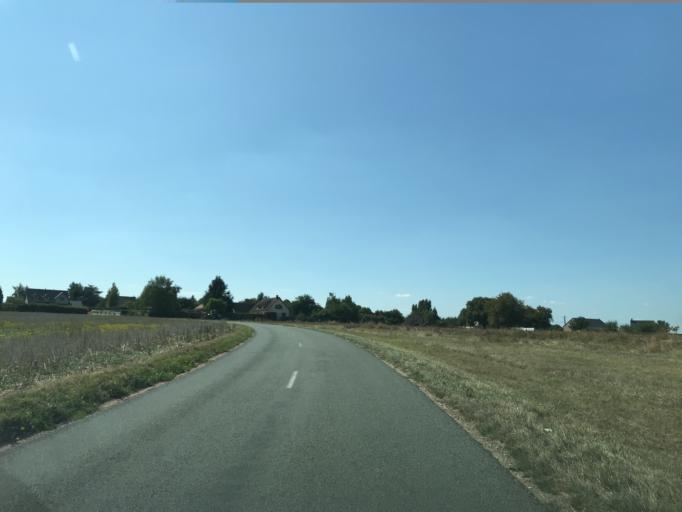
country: FR
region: Haute-Normandie
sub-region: Departement de l'Eure
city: Heudreville-sur-Eure
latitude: 49.0986
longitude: 1.2109
